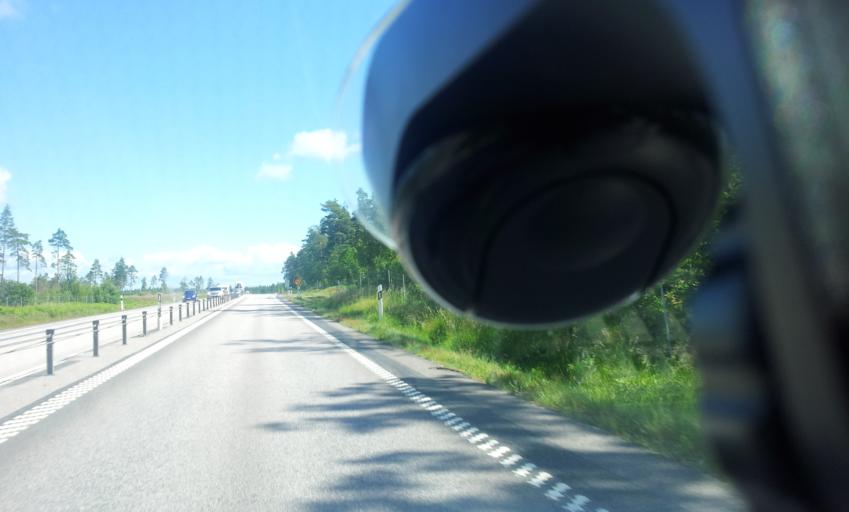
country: SE
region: Kalmar
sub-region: Monsteras Kommun
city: Moensteras
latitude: 57.0953
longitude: 16.4908
